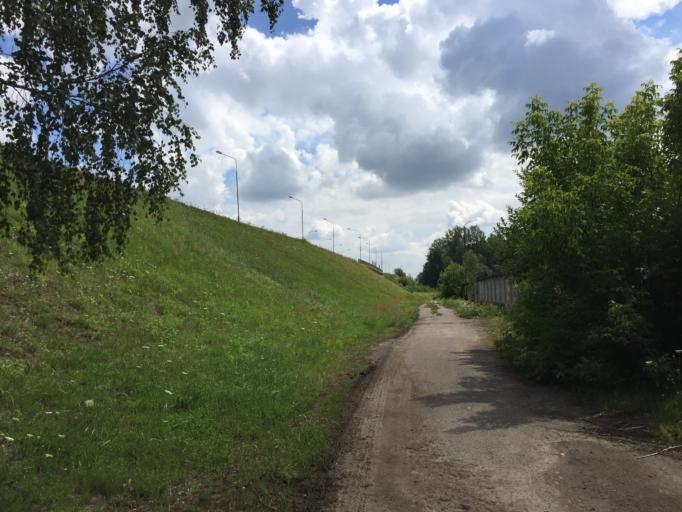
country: LV
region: Ozolnieku
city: Ozolnieki
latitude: 56.6645
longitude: 23.7762
